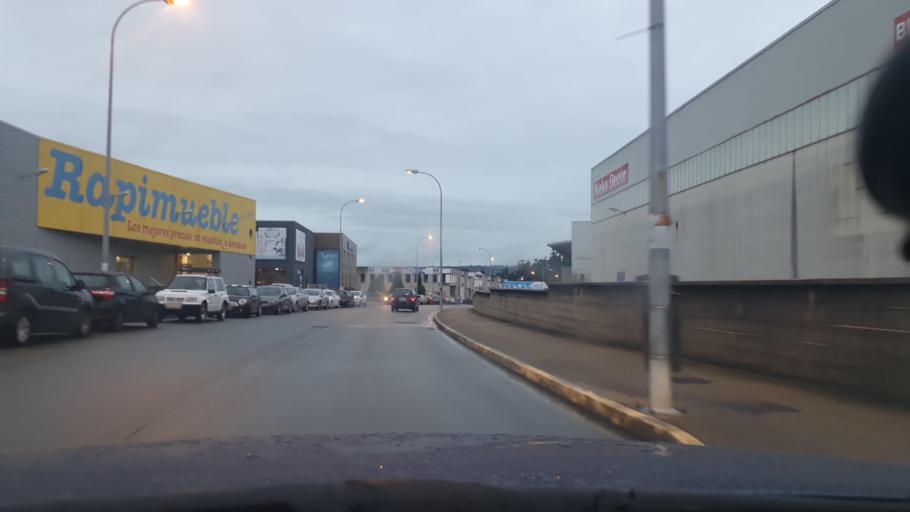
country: ES
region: Galicia
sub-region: Provincia da Coruna
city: Santiago de Compostela
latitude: 42.8503
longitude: -8.5824
